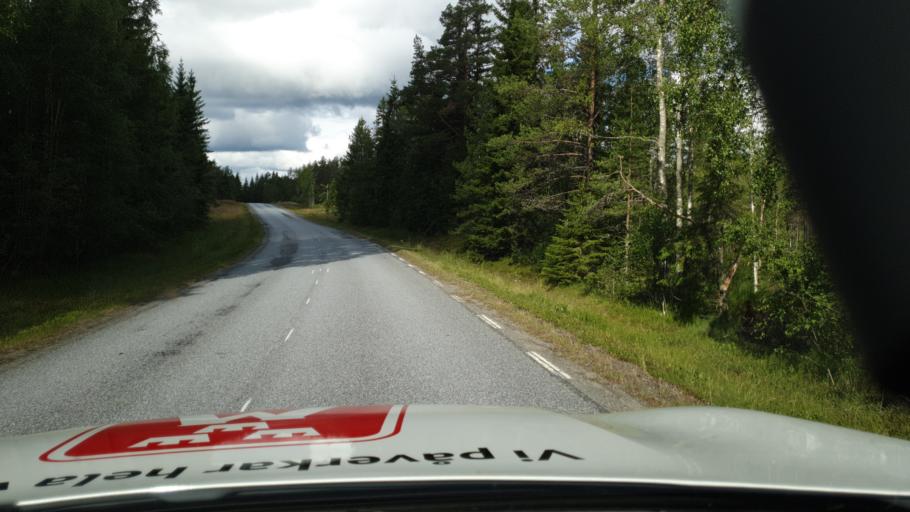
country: SE
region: Vaesterbotten
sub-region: Umea Kommun
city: Hoernefors
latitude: 63.6817
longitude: 20.0437
